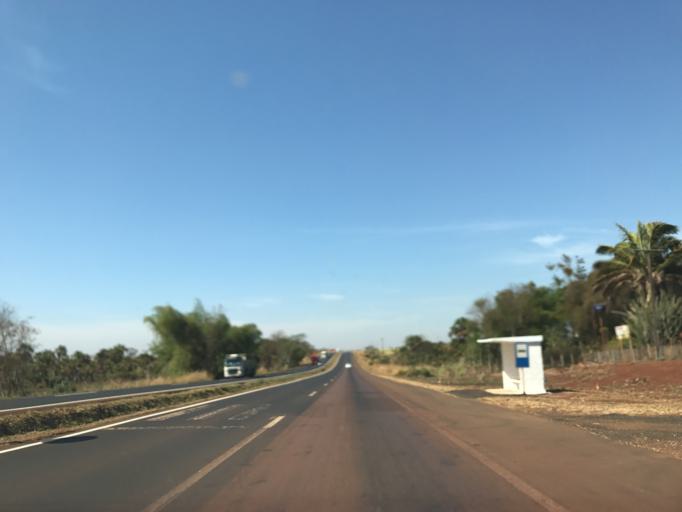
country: BR
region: Goias
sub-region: Itumbiara
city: Itumbiara
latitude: -18.4805
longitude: -49.1886
